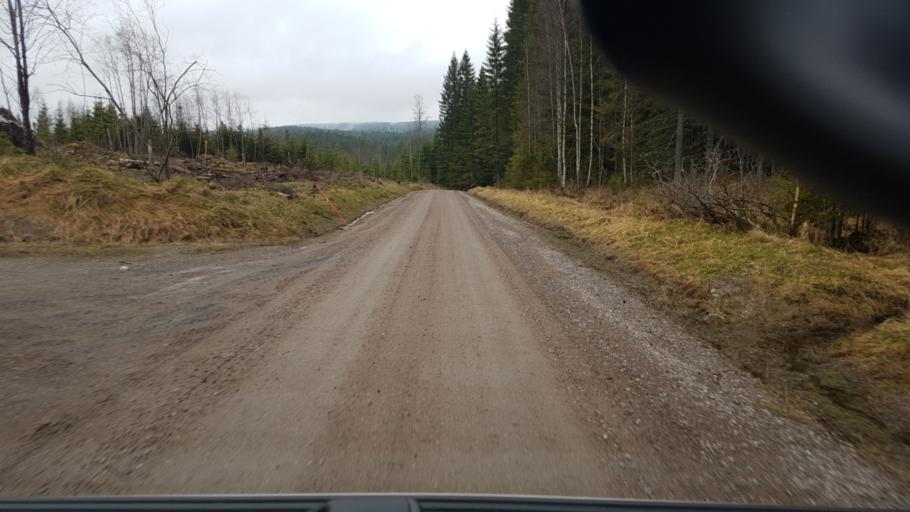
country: SE
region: Vaermland
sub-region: Eda Kommun
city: Charlottenberg
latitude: 60.0351
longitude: 12.5113
